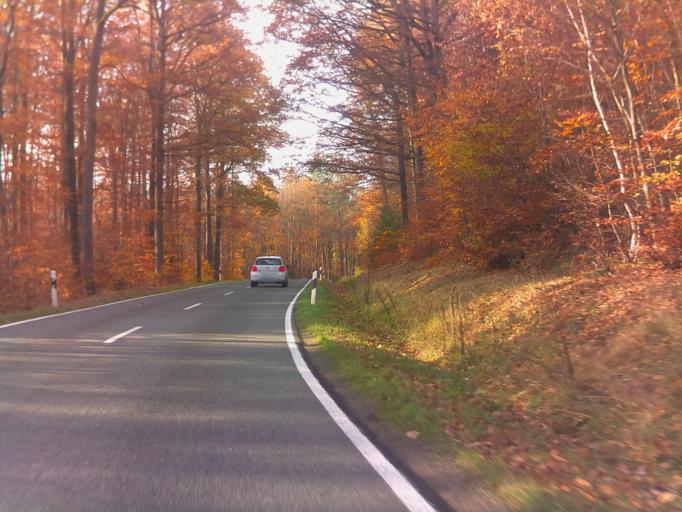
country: DE
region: Bavaria
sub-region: Regierungsbezirk Unterfranken
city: Oberthulba
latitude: 50.2368
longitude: 9.9391
